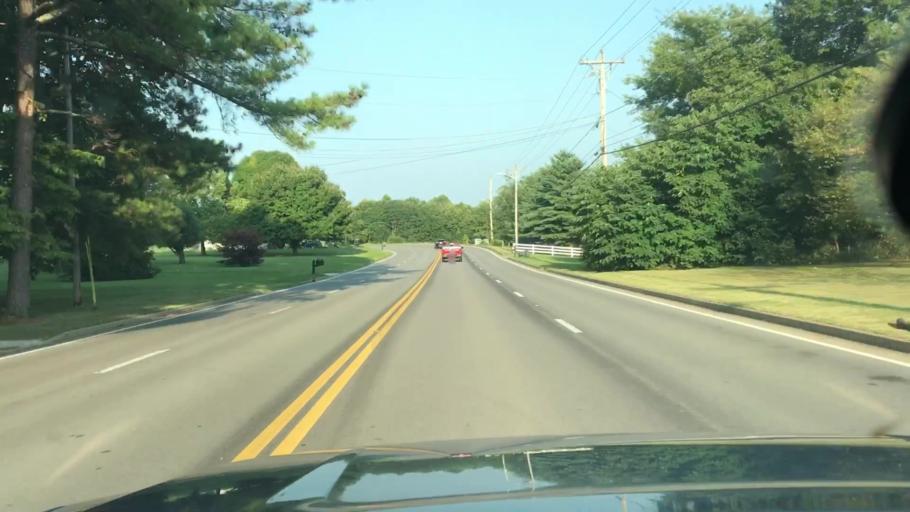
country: US
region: Tennessee
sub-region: Sumner County
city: Portland
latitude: 36.5777
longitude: -86.4823
